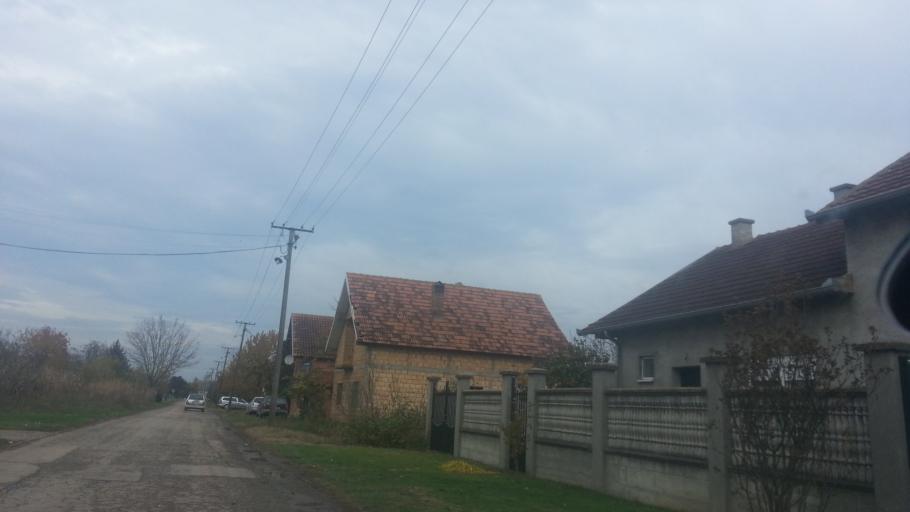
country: RS
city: Golubinci
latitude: 44.9836
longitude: 20.0805
